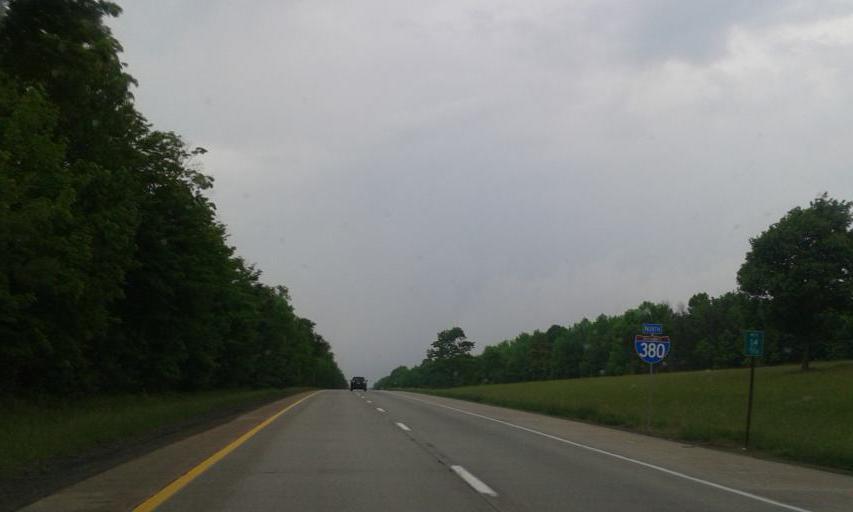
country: US
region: Pennsylvania
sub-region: Lackawanna County
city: Moscow
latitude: 41.2521
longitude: -75.5161
